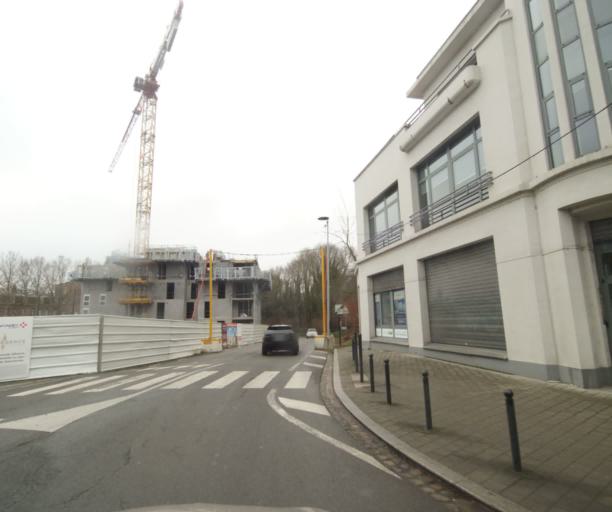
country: FR
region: Nord-Pas-de-Calais
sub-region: Departement du Nord
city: Anzin
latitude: 50.3612
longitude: 3.5173
